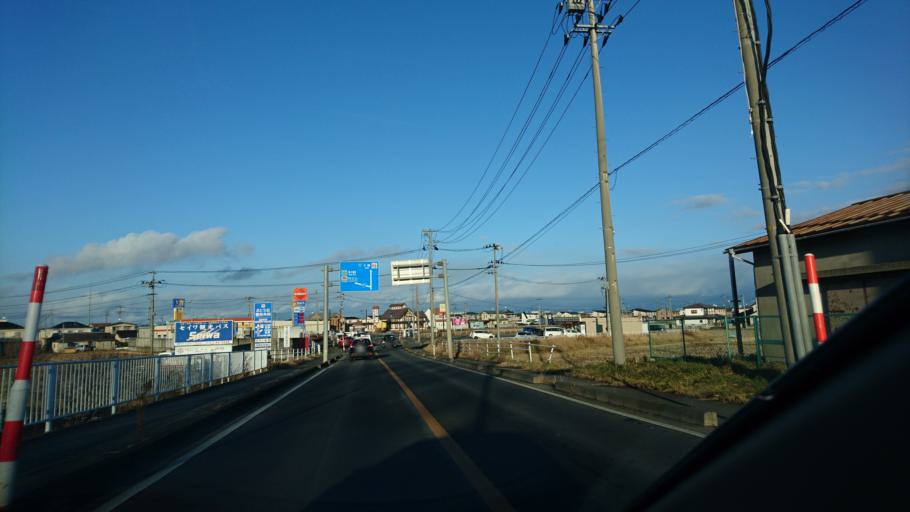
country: JP
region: Miyagi
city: Furukawa
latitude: 38.5598
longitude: 140.8593
